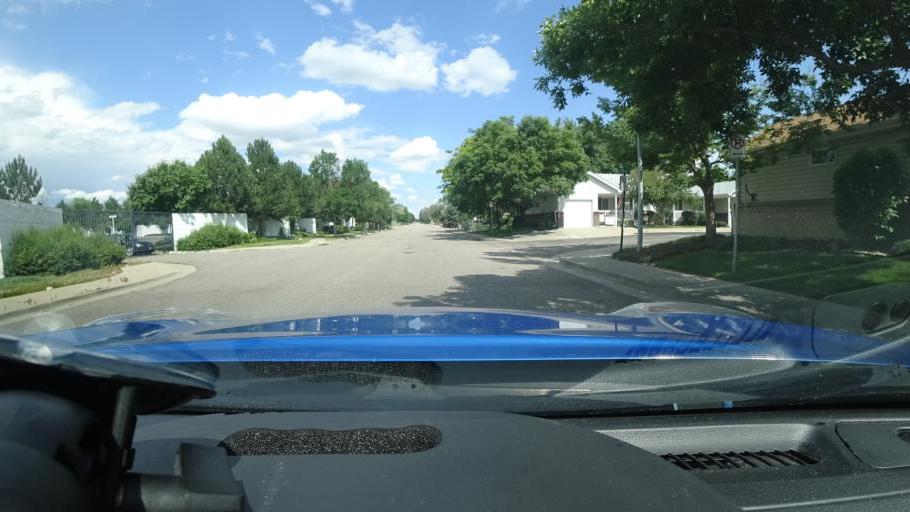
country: US
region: Colorado
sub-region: Adams County
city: Aurora
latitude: 39.6766
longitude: -104.8647
